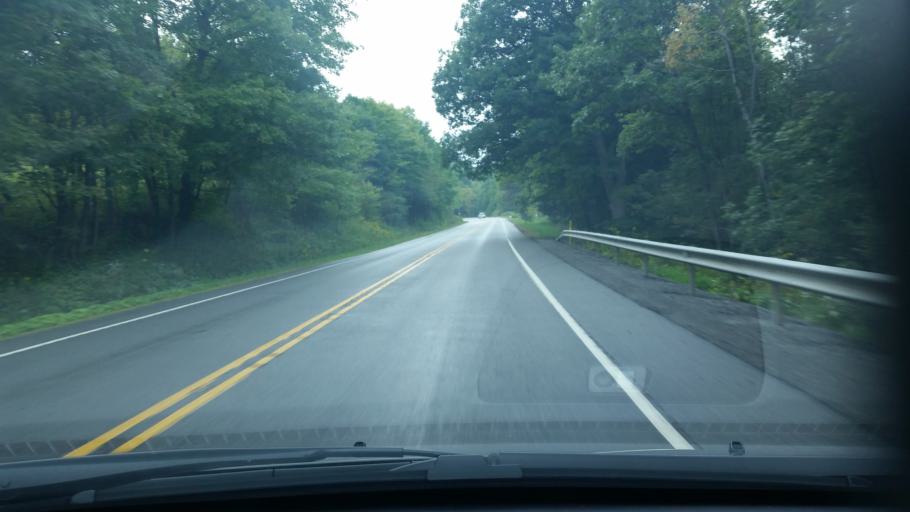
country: US
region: Pennsylvania
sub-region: Clearfield County
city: Shiloh
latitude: 41.0856
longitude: -78.2578
